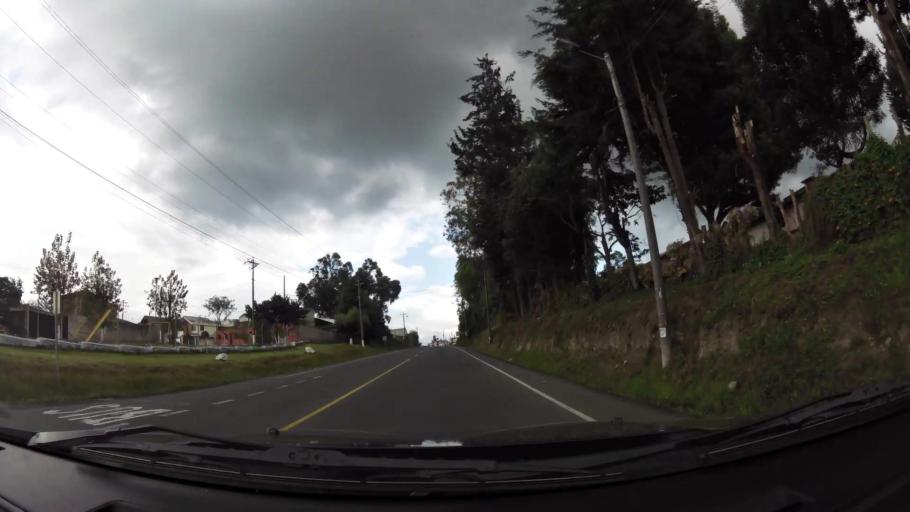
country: EC
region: Pichincha
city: Sangolqui
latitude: -0.3414
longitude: -78.4494
